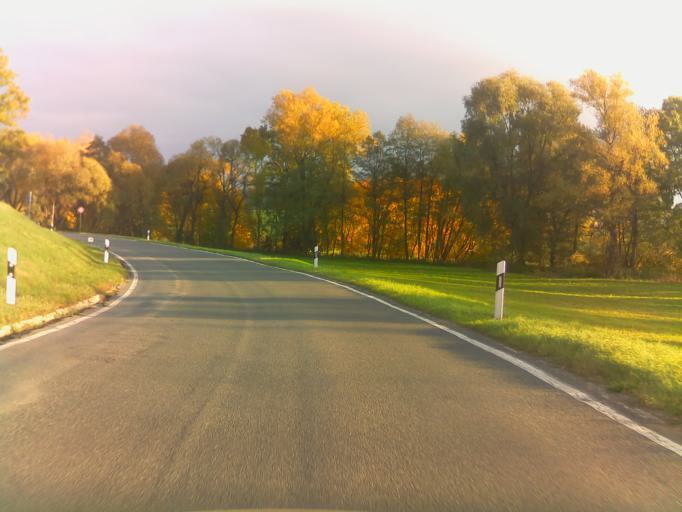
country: DE
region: Thuringia
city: Rittersdorf
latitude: 50.8520
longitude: 11.2670
